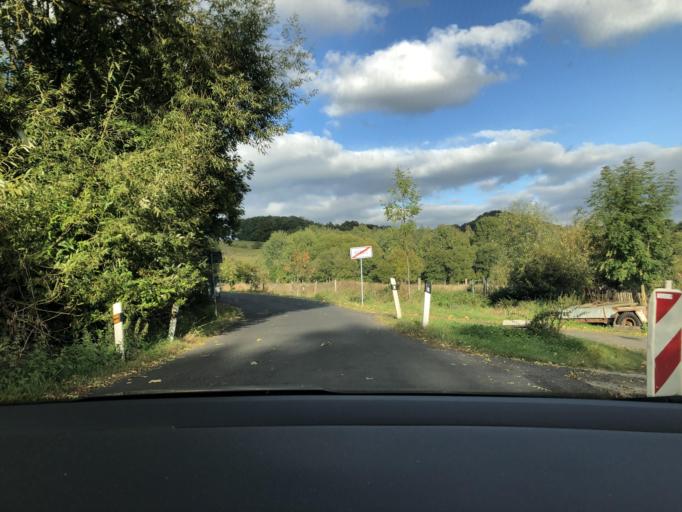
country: CZ
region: Ustecky
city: Zitenice
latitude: 50.6067
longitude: 14.1628
